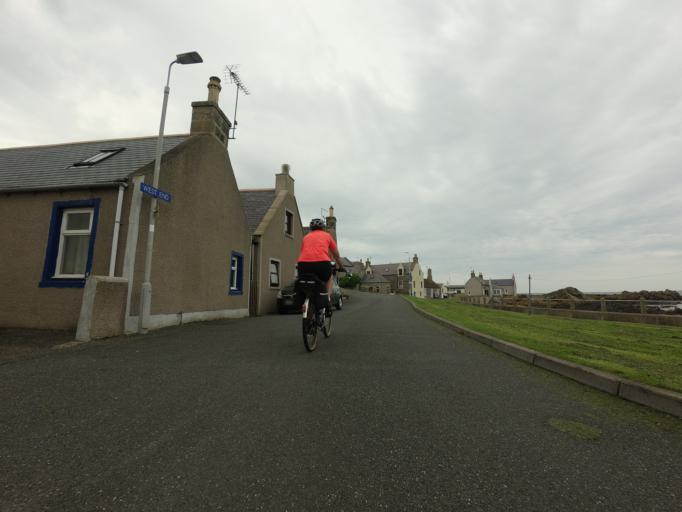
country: GB
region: Scotland
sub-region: Aberdeenshire
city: Whitehills
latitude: 57.6774
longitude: -2.5852
